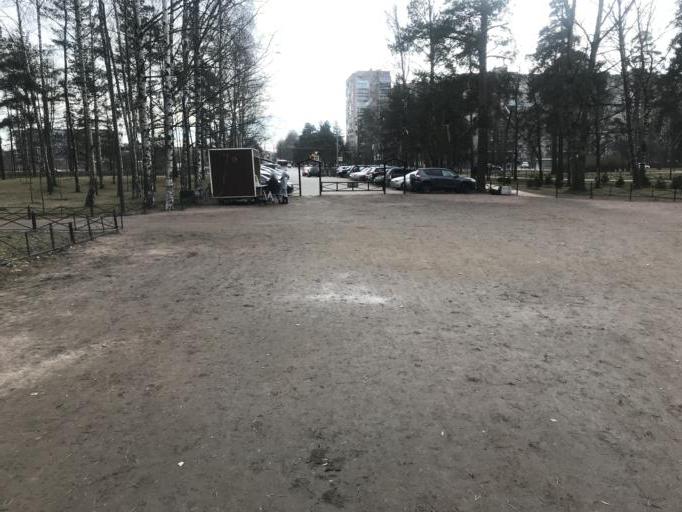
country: RU
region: St.-Petersburg
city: Sosnovka
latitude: 60.0142
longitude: 30.3523
